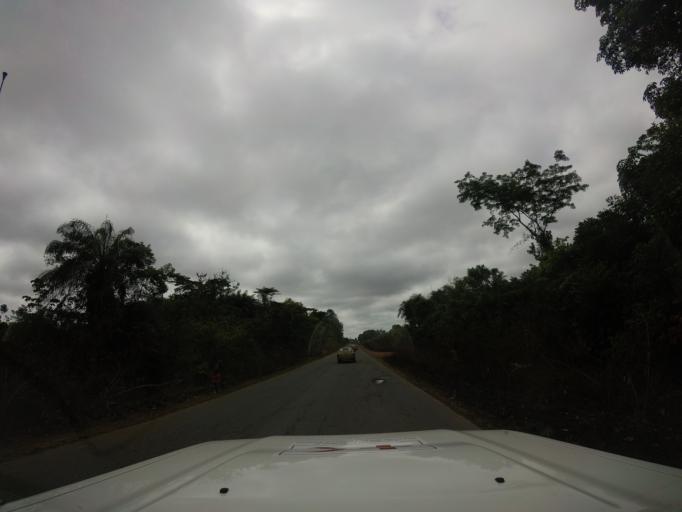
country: LR
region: Montserrado
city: Monrovia
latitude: 6.5543
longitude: -10.8660
